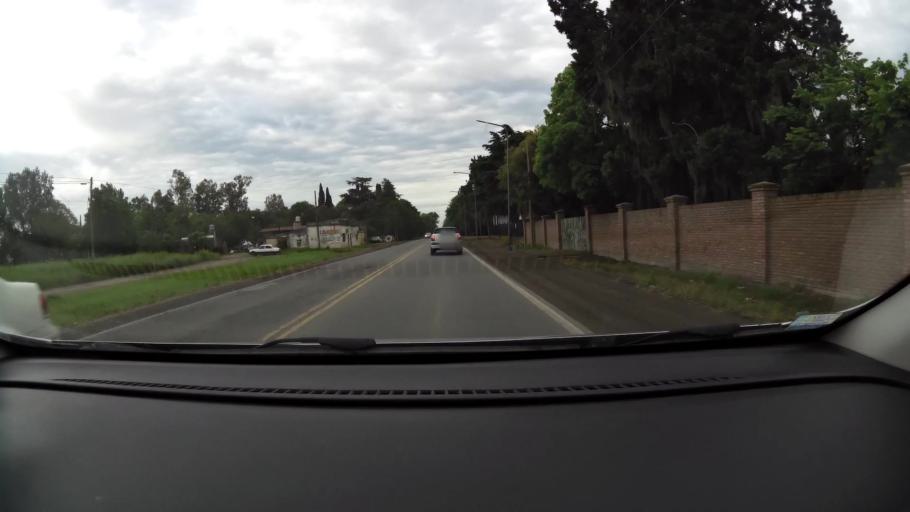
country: AR
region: Buenos Aires
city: San Nicolas de los Arroyos
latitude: -33.3820
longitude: -60.2132
